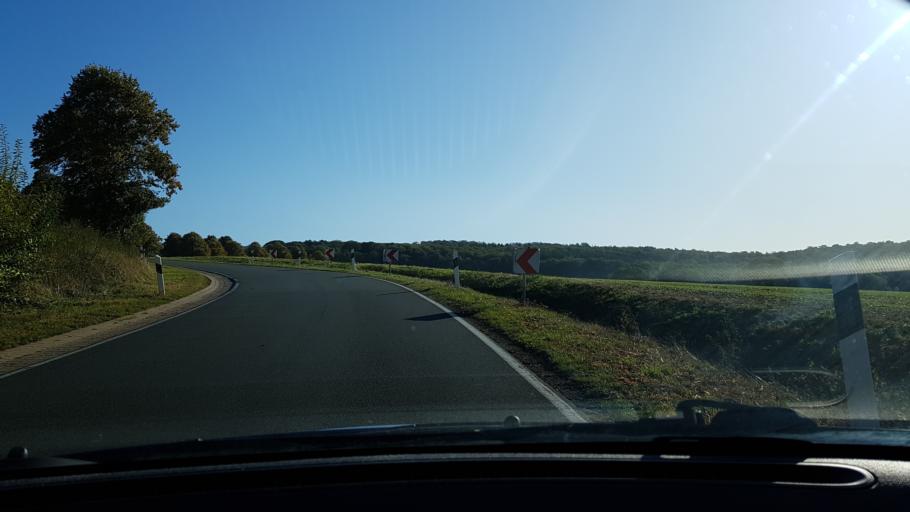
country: DE
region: Lower Saxony
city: Messenkamp
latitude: 52.2563
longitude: 9.3995
